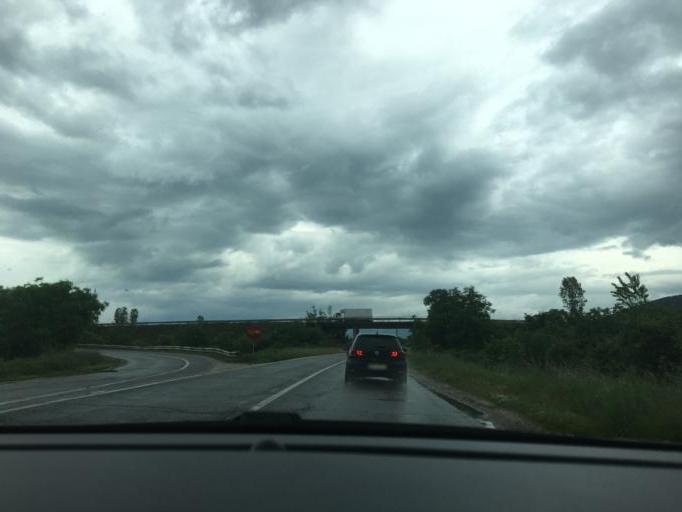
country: MK
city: Misleshevo
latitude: 41.1606
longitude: 20.7508
